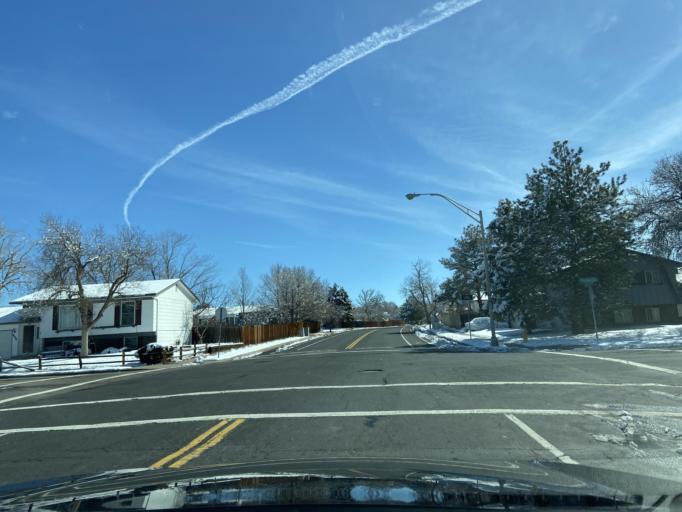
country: US
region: Colorado
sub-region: Adams County
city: Aurora
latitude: 39.7038
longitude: -104.8554
